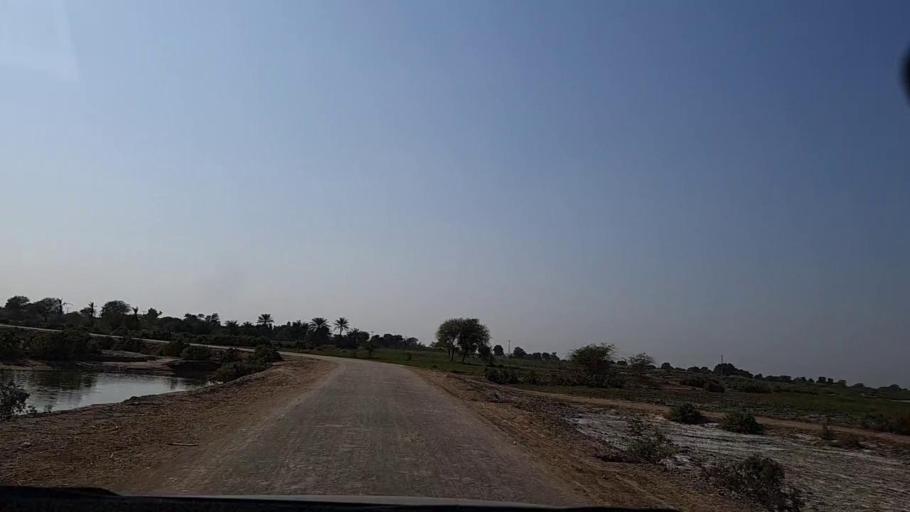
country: PK
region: Sindh
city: Digri
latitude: 25.1736
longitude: 69.0455
